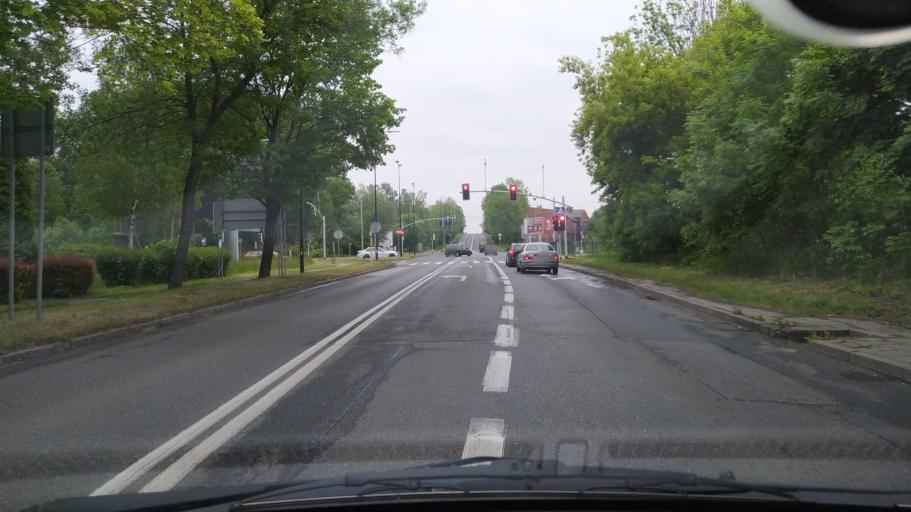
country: PL
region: Silesian Voivodeship
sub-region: Gliwice
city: Gliwice
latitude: 50.2737
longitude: 18.7011
